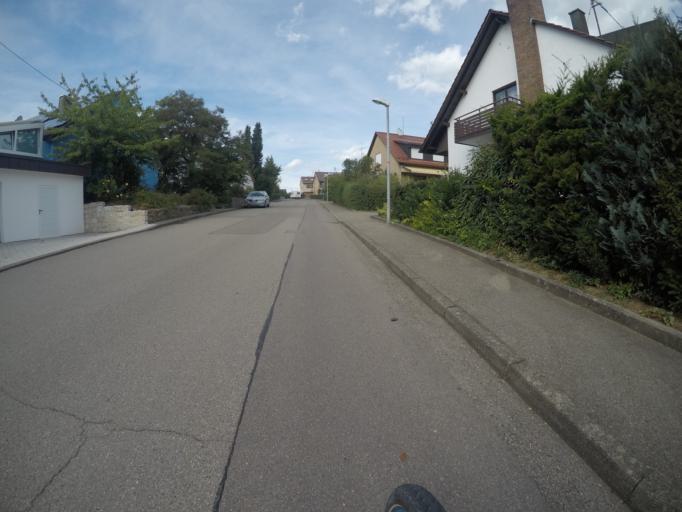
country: DE
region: Baden-Wuerttemberg
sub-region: Regierungsbezirk Stuttgart
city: Gartringen
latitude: 48.6403
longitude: 8.8893
